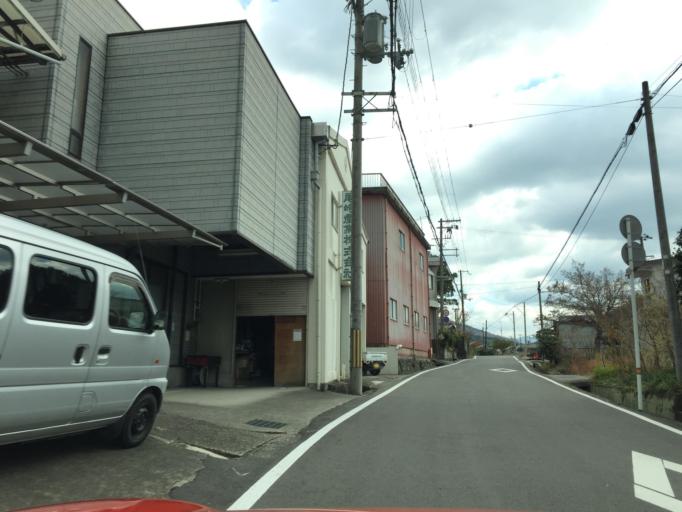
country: JP
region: Wakayama
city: Kainan
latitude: 34.1643
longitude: 135.2882
